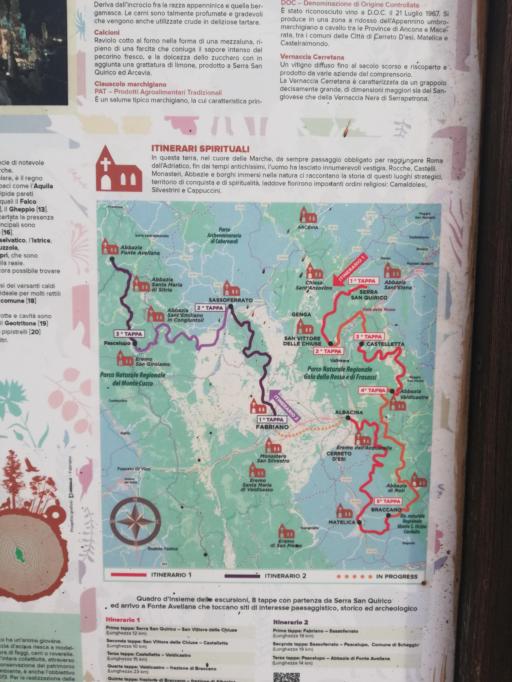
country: IT
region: The Marches
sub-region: Provincia di Ancona
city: Genga
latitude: 43.4025
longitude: 12.9712
